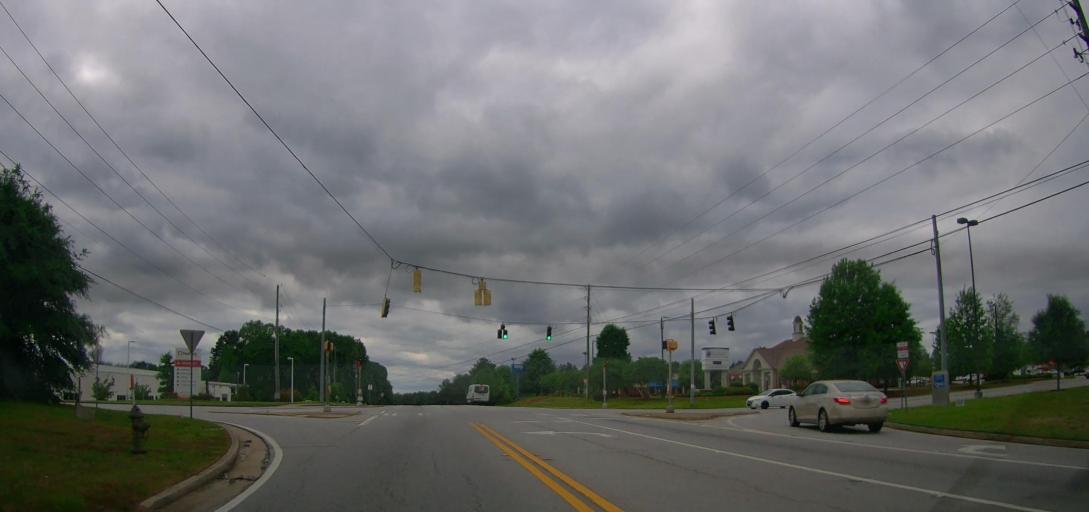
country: US
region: Georgia
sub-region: Walton County
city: Monroe
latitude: 33.7983
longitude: -83.7461
